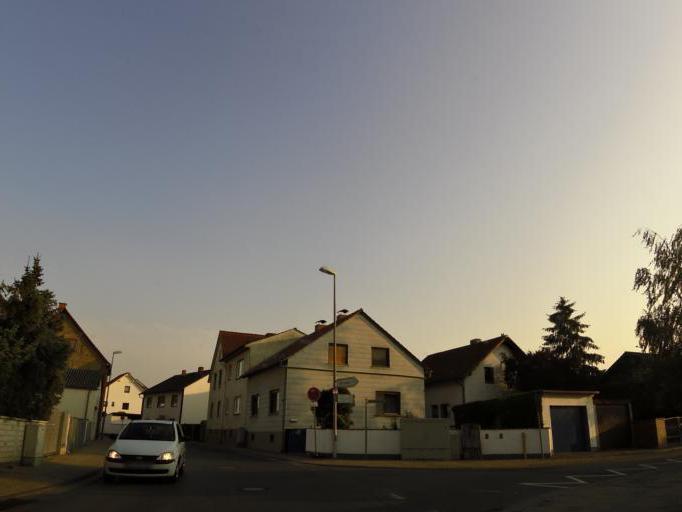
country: DE
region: Hesse
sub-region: Regierungsbezirk Darmstadt
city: Buttelborn
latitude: 49.9276
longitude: 8.5447
